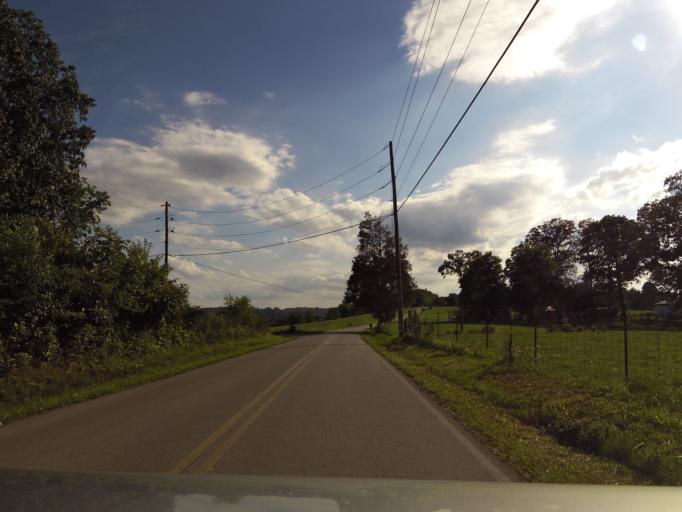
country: US
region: Tennessee
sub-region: Loudon County
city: Greenback
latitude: 35.6704
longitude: -84.0646
